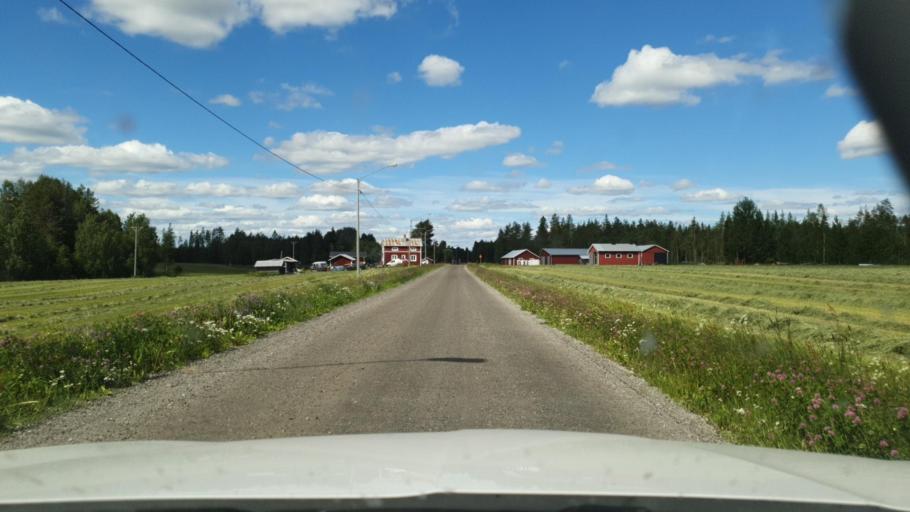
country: SE
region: Vaesterbotten
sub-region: Skelleftea Kommun
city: Backa
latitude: 65.1829
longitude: 21.0680
